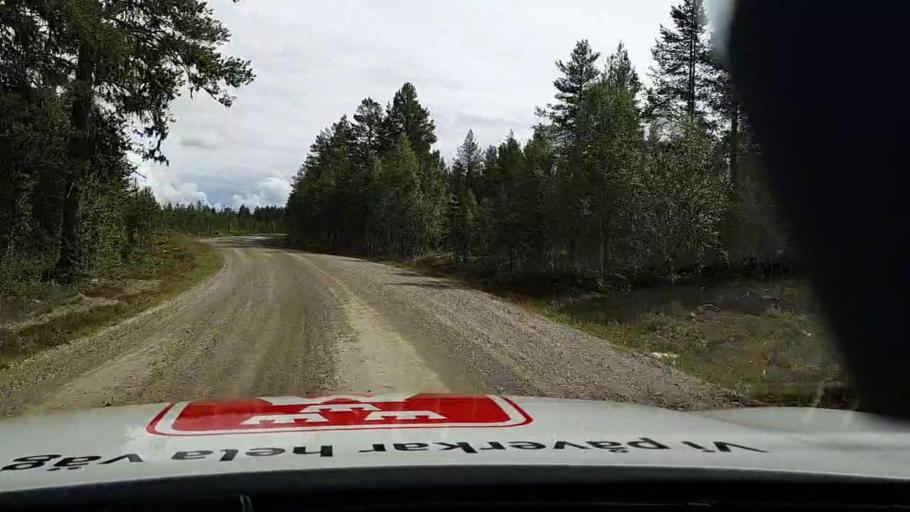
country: SE
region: Jaemtland
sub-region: Are Kommun
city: Jarpen
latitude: 62.5050
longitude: 13.4989
